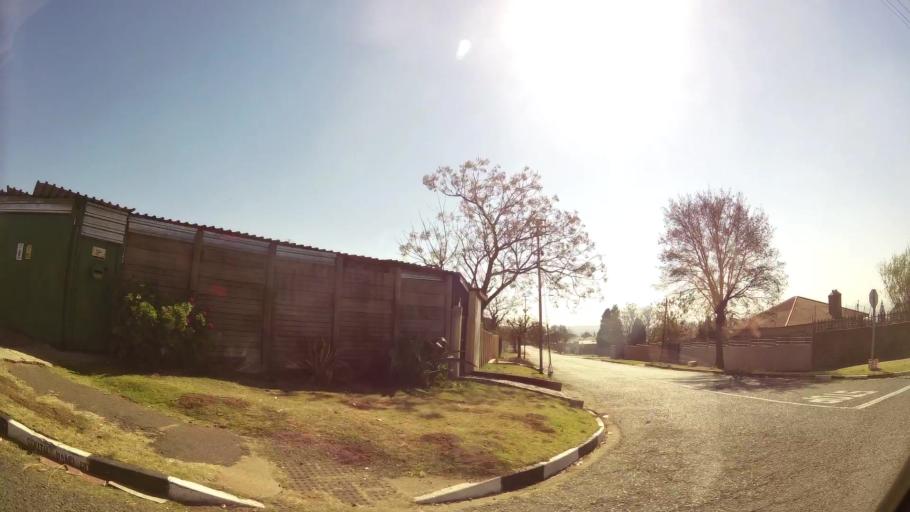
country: ZA
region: Gauteng
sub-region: City of Johannesburg Metropolitan Municipality
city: Johannesburg
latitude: -26.2560
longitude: 28.0898
